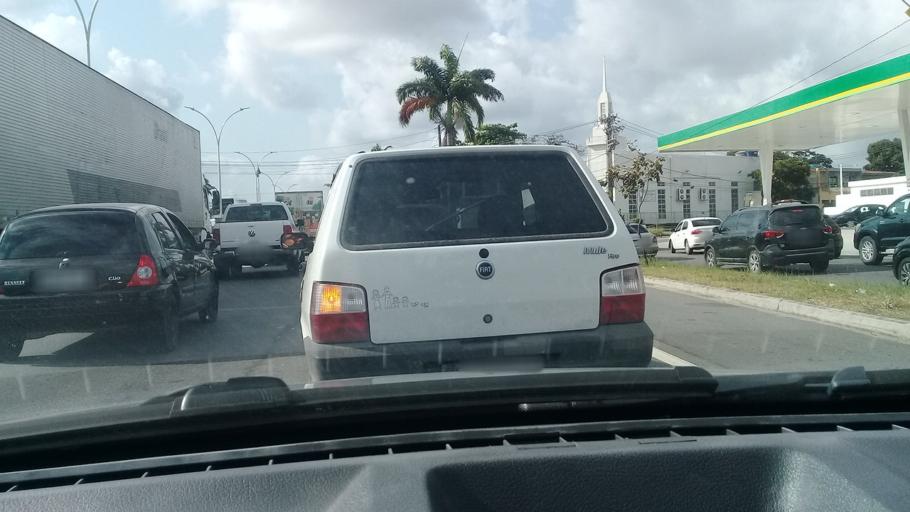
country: BR
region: Pernambuco
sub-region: Recife
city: Recife
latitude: -8.0336
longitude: -34.9418
